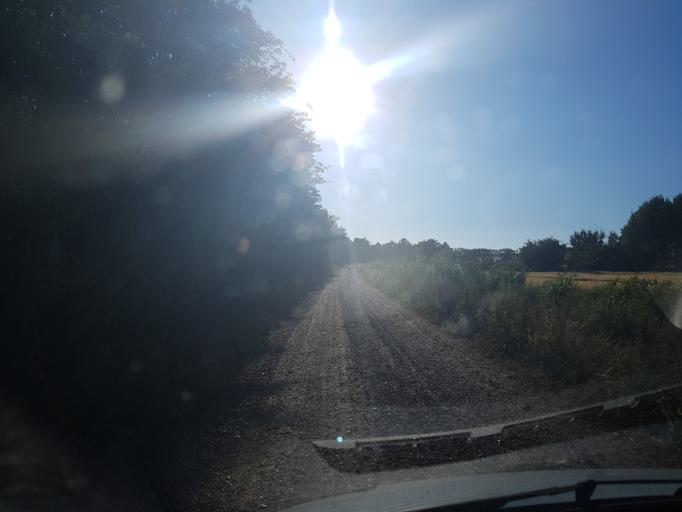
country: DK
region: South Denmark
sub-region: Esbjerg Kommune
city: Esbjerg
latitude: 55.4937
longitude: 8.5152
